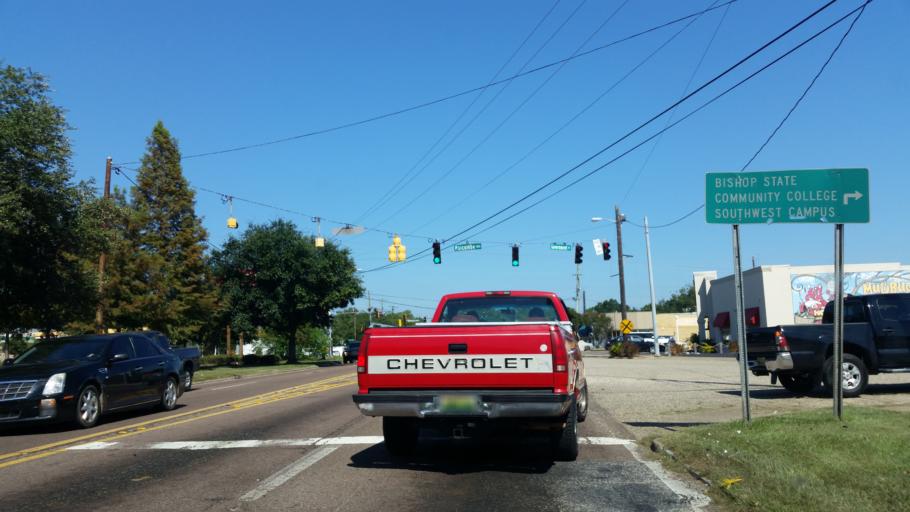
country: US
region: Alabama
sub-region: Mobile County
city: Mobile
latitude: 30.6754
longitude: -88.0883
